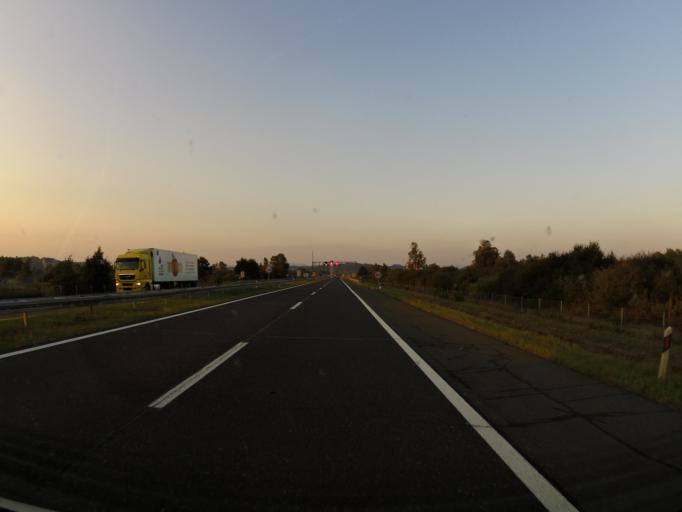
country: HR
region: Zagrebacka
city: Jakovlje
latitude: 45.9899
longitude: 15.8603
